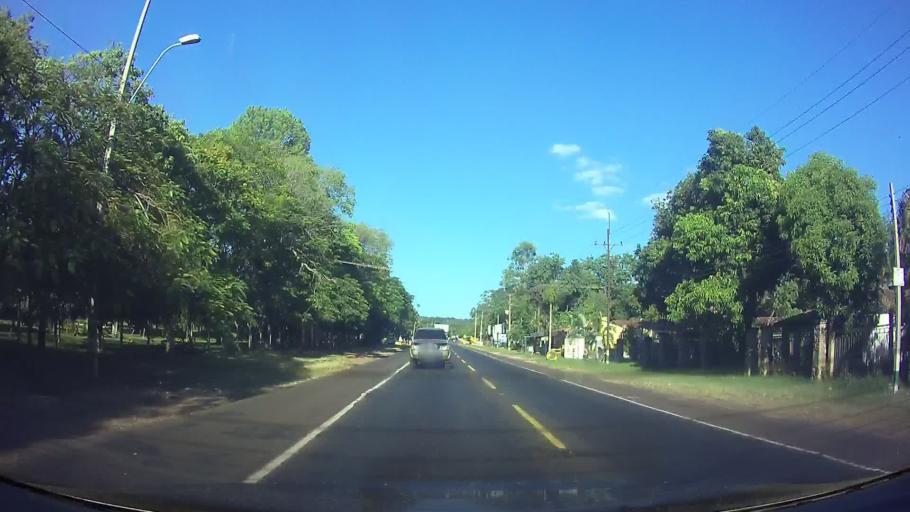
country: PY
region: Central
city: Ypacarai
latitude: -25.3739
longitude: -57.2253
